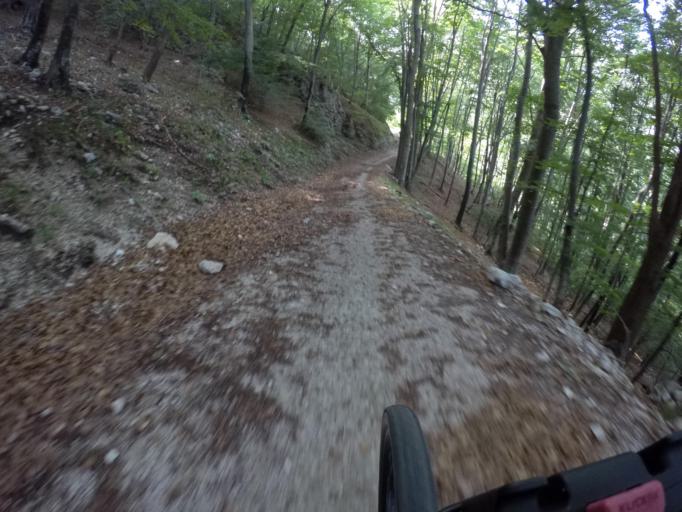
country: IT
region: Friuli Venezia Giulia
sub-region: Provincia di Udine
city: Resiutta
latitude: 46.3264
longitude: 13.2180
